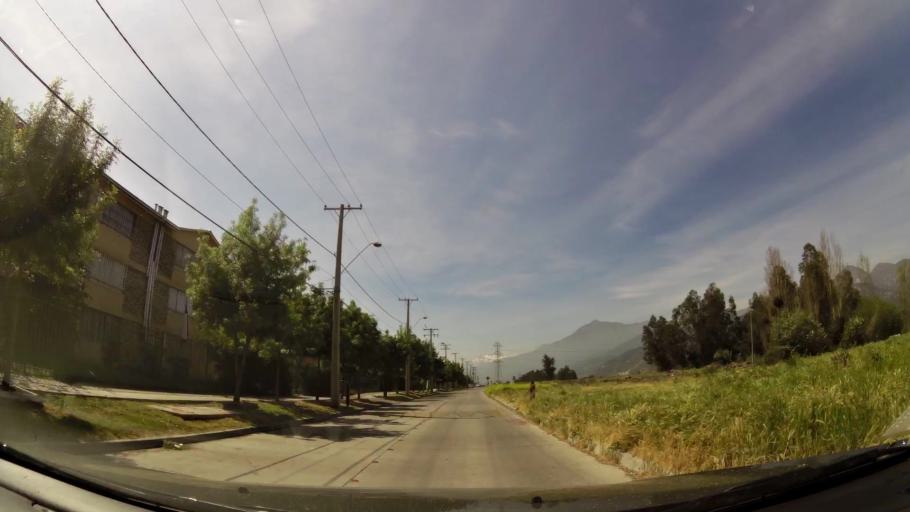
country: CL
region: Santiago Metropolitan
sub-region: Provincia de Cordillera
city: Puente Alto
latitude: -33.6156
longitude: -70.5528
